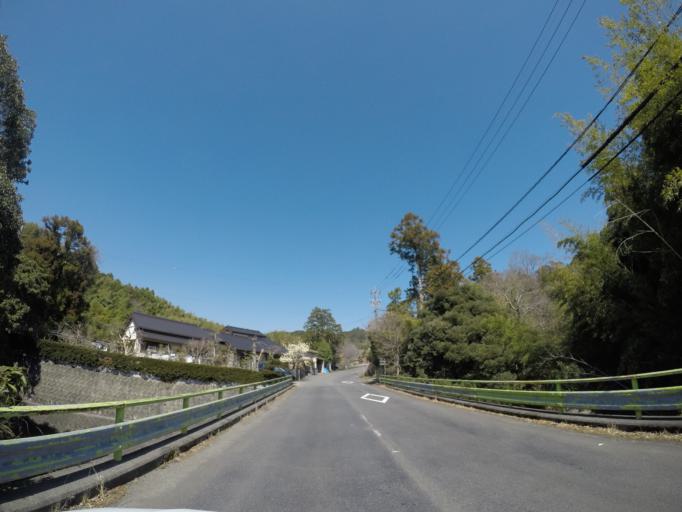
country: JP
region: Shizuoka
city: Kanaya
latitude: 34.7911
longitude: 138.1259
